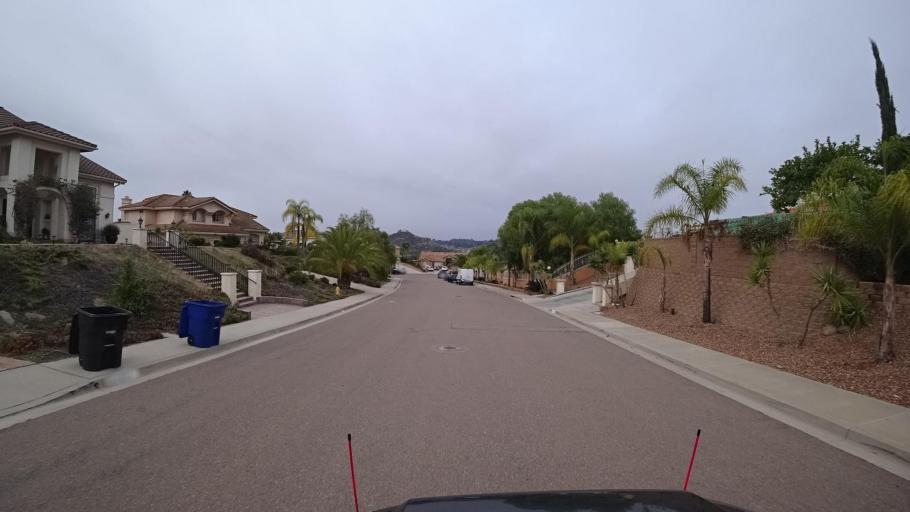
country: US
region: California
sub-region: San Diego County
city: Rancho San Diego
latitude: 32.7610
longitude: -116.9130
